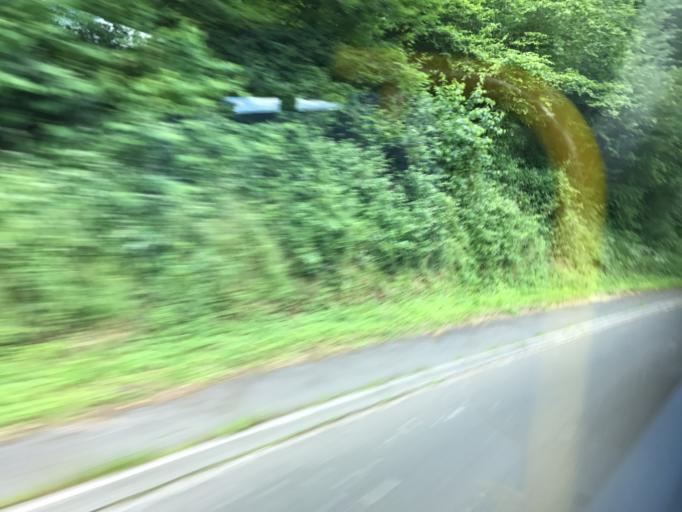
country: DE
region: Hesse
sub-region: Regierungsbezirk Darmstadt
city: Schlangenbad
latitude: 50.0670
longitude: 8.1087
